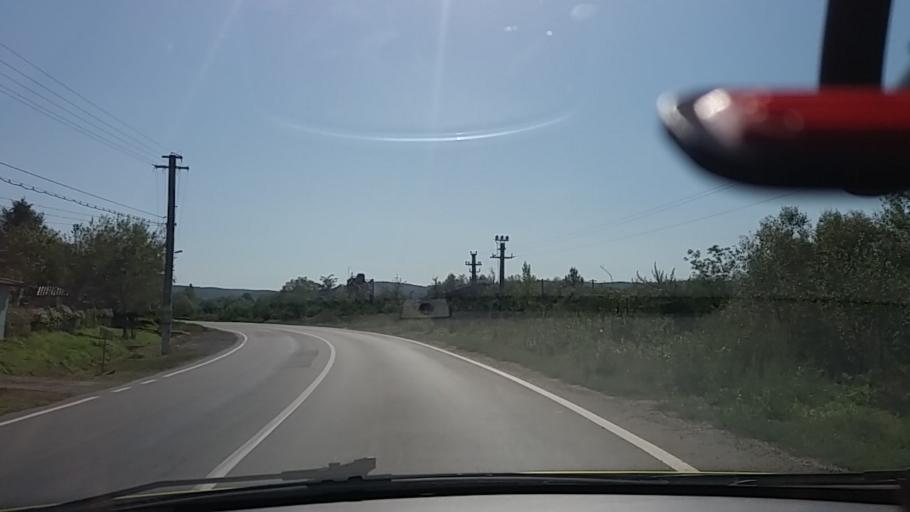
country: RO
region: Arad
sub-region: Comuna Conop
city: Conop
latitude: 46.1060
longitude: 21.8678
